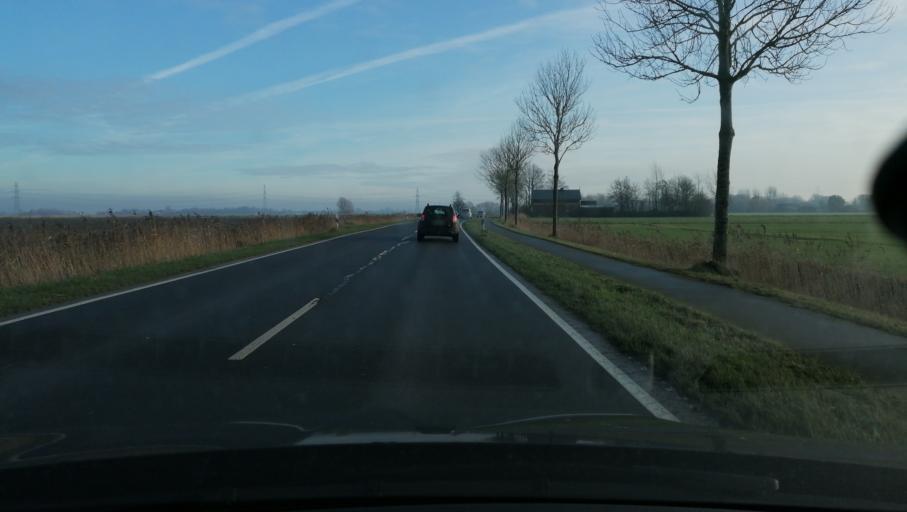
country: DE
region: Schleswig-Holstein
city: Epenwohrden
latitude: 54.1120
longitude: 9.0196
